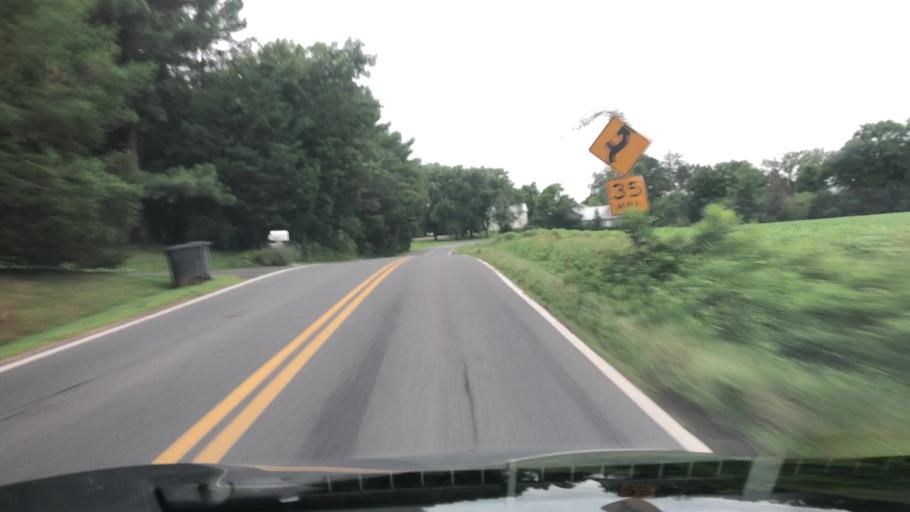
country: US
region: Virginia
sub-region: Prince William County
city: Nokesville
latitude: 38.5838
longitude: -77.6105
